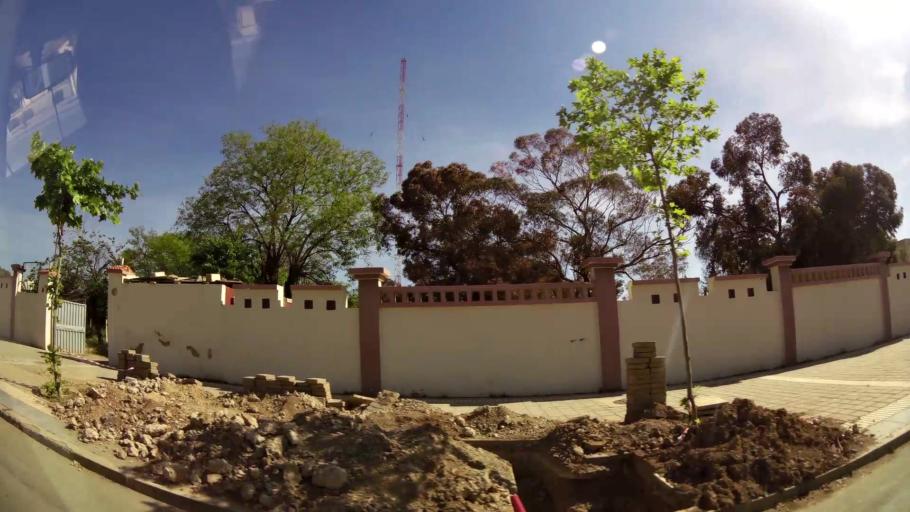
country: MA
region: Oriental
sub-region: Oujda-Angad
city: Oujda
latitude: 34.6643
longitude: -1.9080
